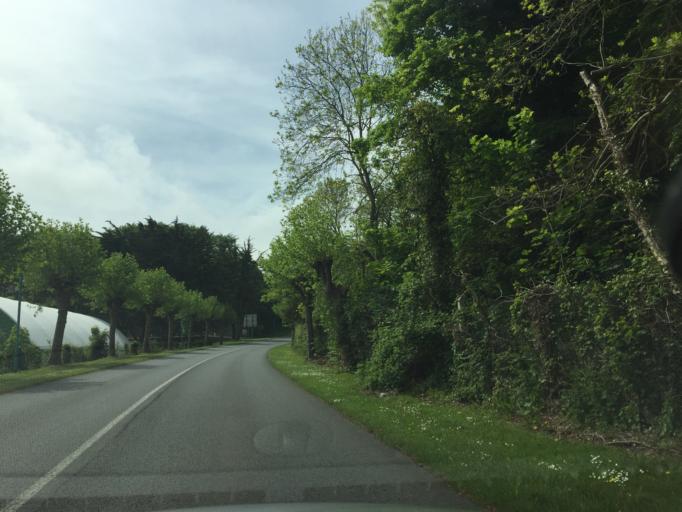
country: FR
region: Brittany
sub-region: Departement des Cotes-d'Armor
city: Saint-Cast-le-Guildo
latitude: 48.6239
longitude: -2.2521
